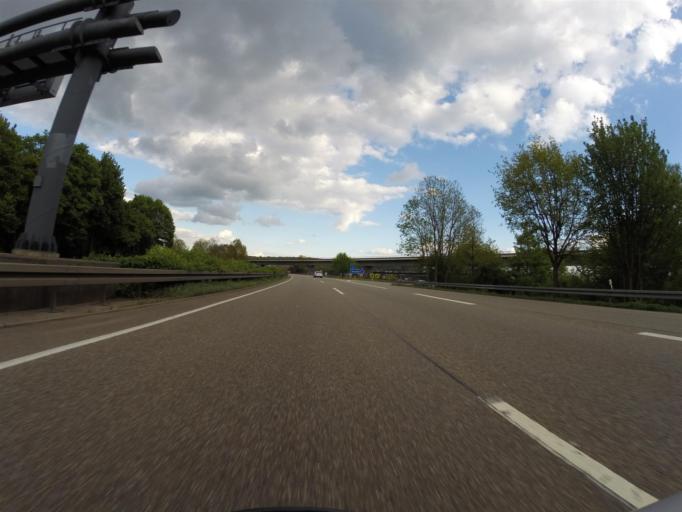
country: FR
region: Lorraine
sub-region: Departement de la Moselle
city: Alsting
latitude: 49.2086
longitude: 7.0244
